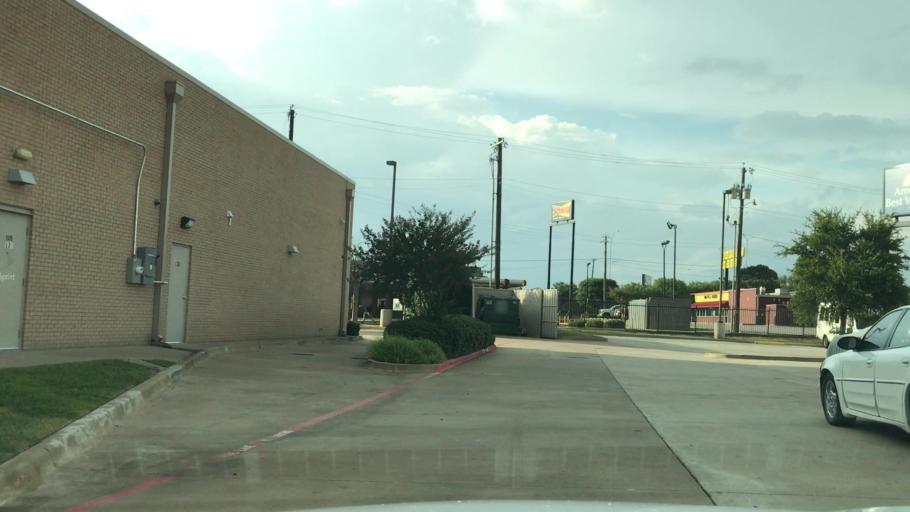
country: US
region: Texas
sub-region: Dallas County
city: Sunnyvale
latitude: 32.8386
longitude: -96.5948
